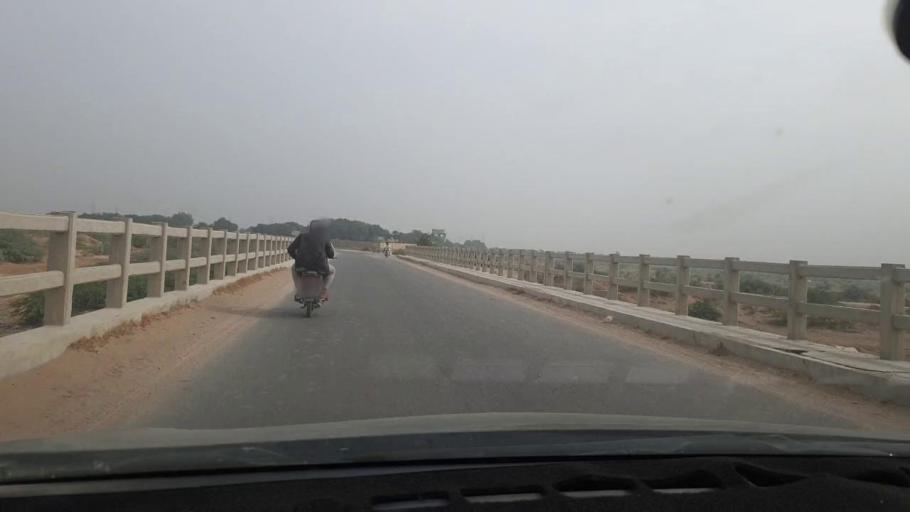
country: PK
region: Sindh
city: Malir Cantonment
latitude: 24.9143
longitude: 67.2670
